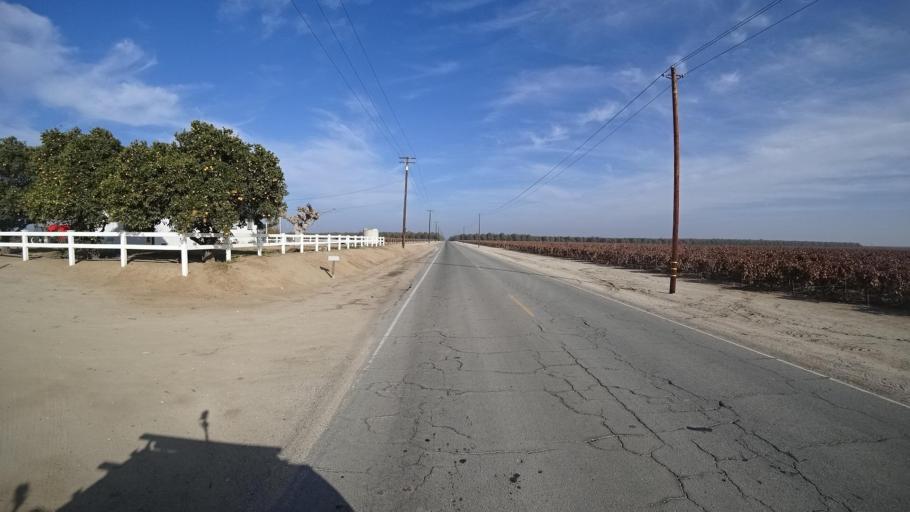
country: US
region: California
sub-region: Kern County
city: McFarland
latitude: 35.6121
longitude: -119.2044
